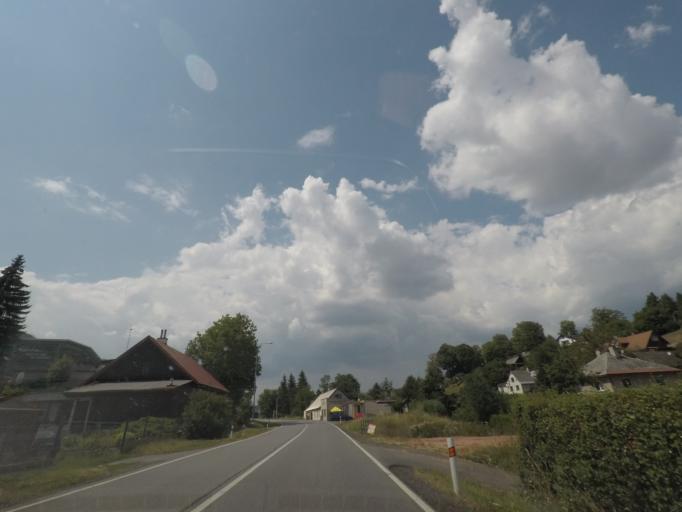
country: CZ
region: Kralovehradecky
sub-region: Okres Jicin
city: Pecka
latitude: 50.5310
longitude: 15.6158
